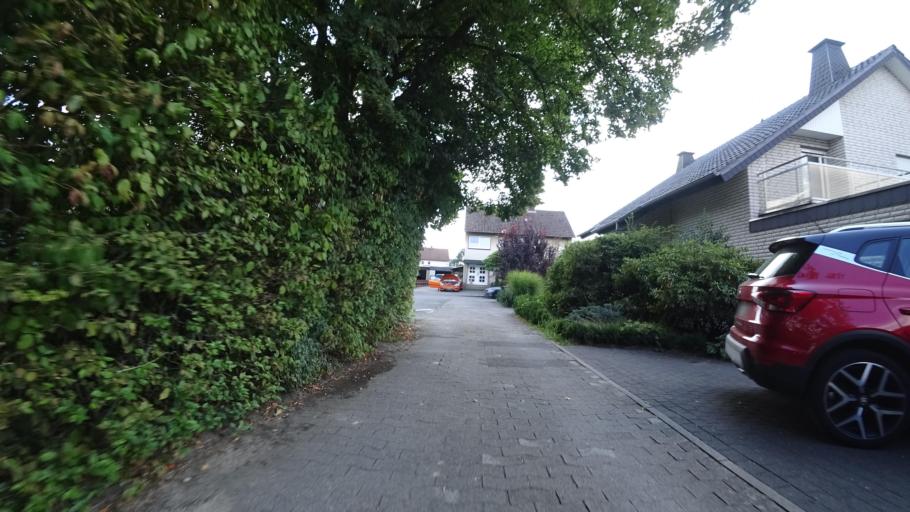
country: DE
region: North Rhine-Westphalia
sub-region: Regierungsbezirk Detmold
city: Guetersloh
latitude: 51.8749
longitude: 8.4314
